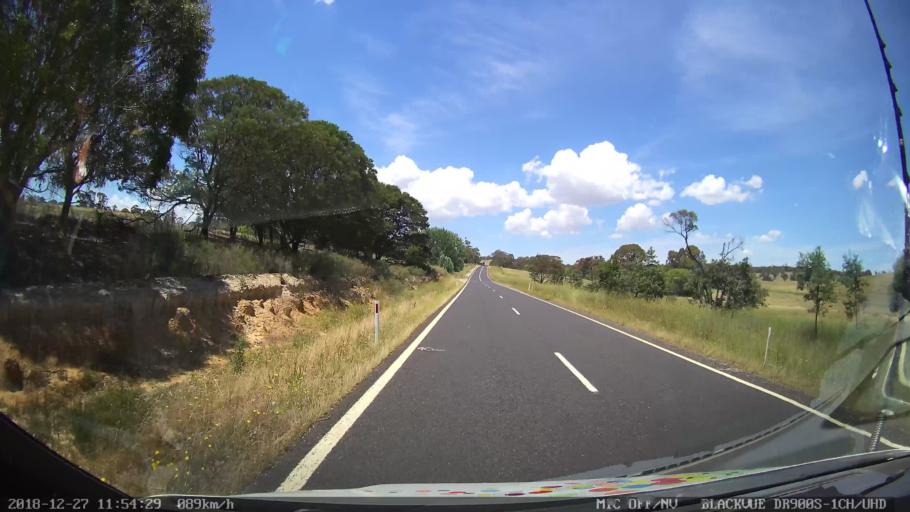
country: AU
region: New South Wales
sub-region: Blayney
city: Blayney
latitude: -33.6754
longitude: 149.4023
